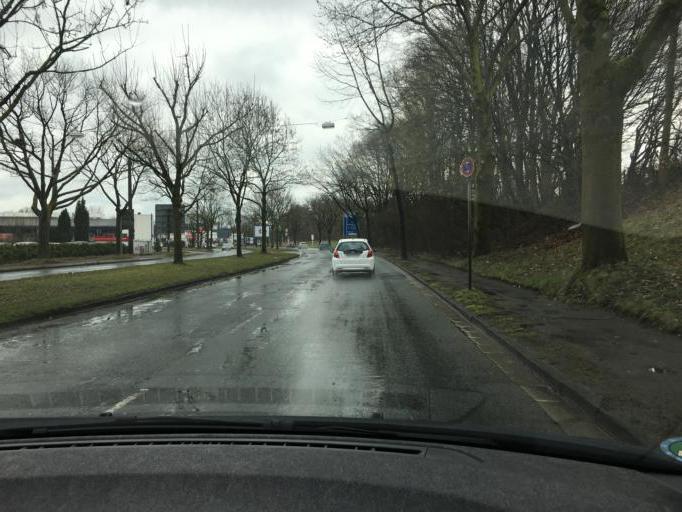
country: DE
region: North Rhine-Westphalia
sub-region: Regierungsbezirk Arnsberg
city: Bochum
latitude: 51.4936
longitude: 7.2579
